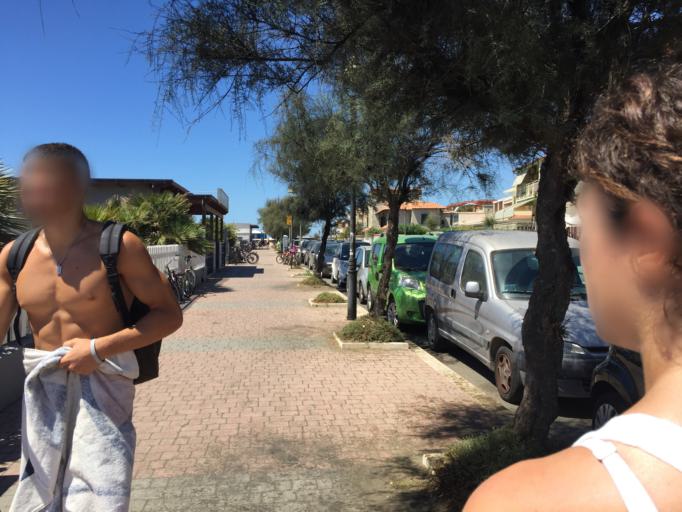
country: IT
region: Latium
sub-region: Citta metropolitana di Roma Capitale
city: Ladispoli
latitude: 41.9508
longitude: 12.0693
